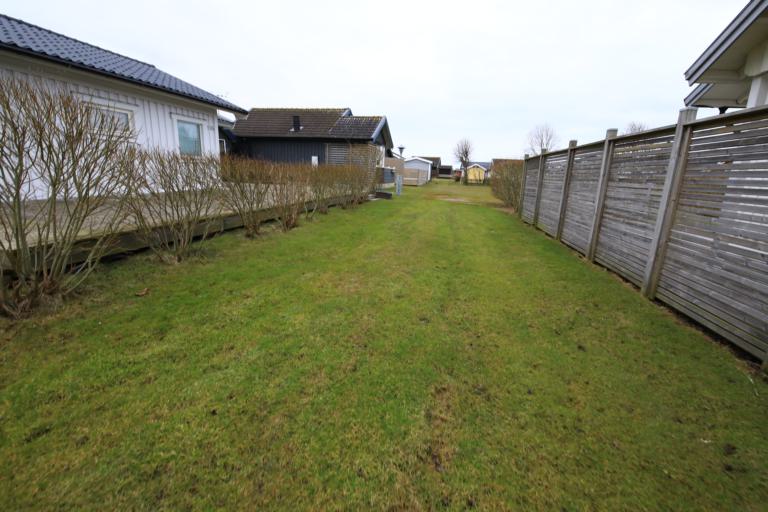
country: SE
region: Halland
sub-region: Varbergs Kommun
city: Traslovslage
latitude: 57.0704
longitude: 12.2771
